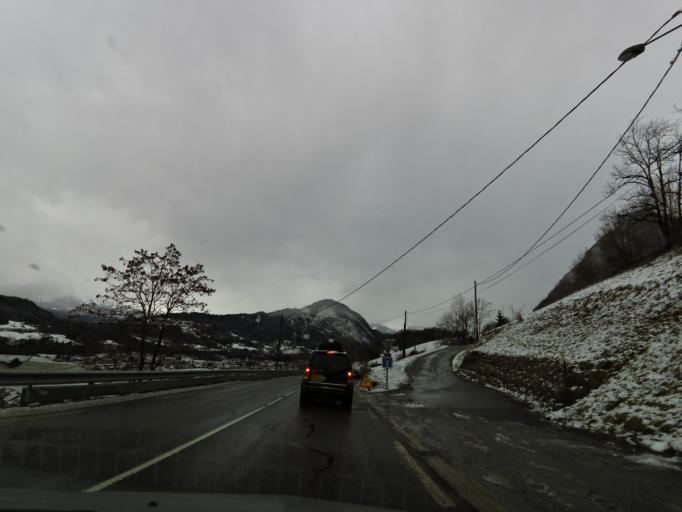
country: FR
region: Rhone-Alpes
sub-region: Departement de la Haute-Savoie
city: Taninges
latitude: 46.1101
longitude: 6.6077
